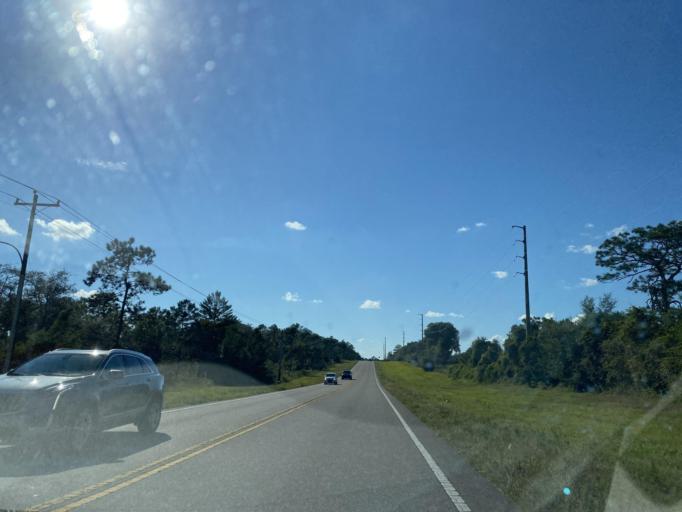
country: US
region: Florida
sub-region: Marion County
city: Ocala
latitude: 29.0521
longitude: -82.2643
